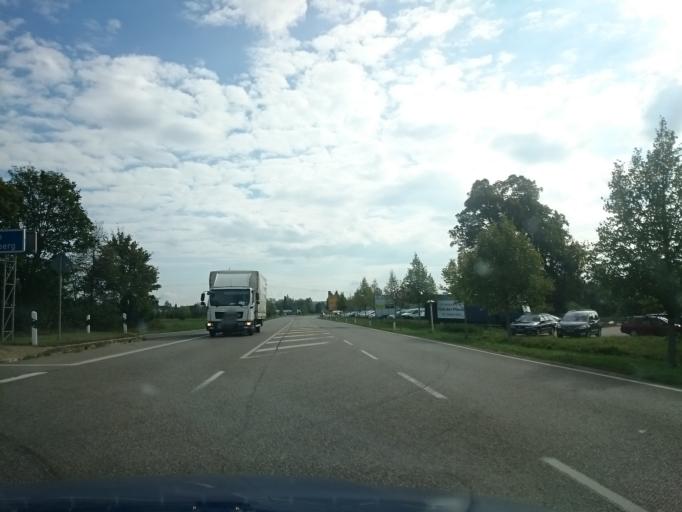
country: DE
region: Bavaria
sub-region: Regierungsbezirk Mittelfranken
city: Allersberg
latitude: 49.2486
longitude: 11.2179
